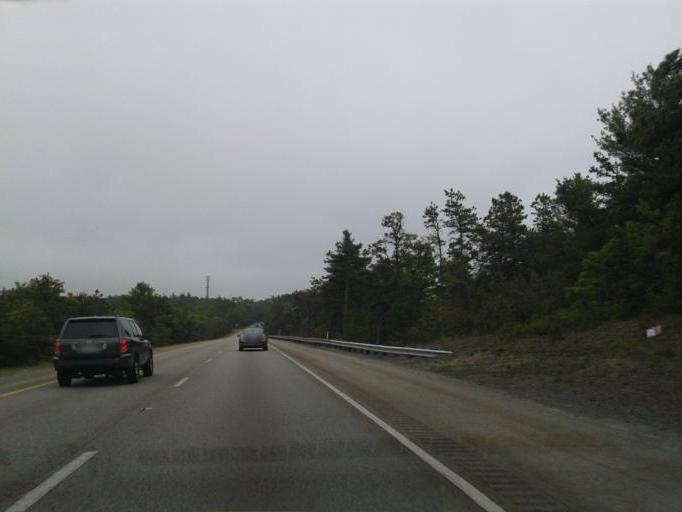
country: US
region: Massachusetts
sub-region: Plymouth County
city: White Island Shores
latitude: 41.8577
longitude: -70.5843
